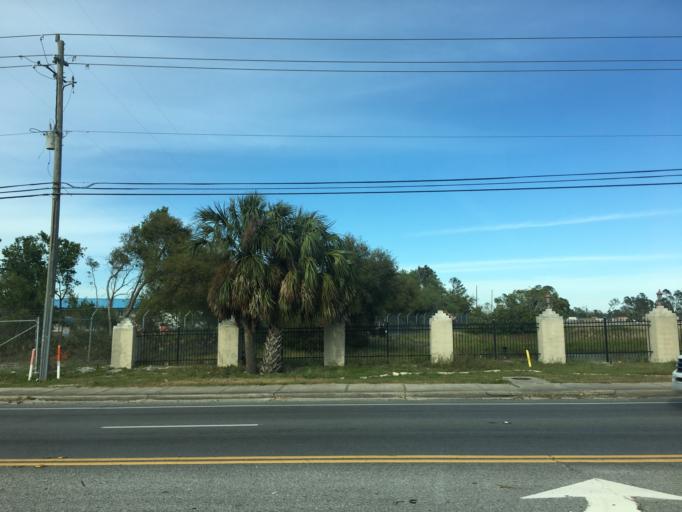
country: US
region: Florida
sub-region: Bay County
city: Upper Grand Lagoon
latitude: 30.1688
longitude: -85.7579
